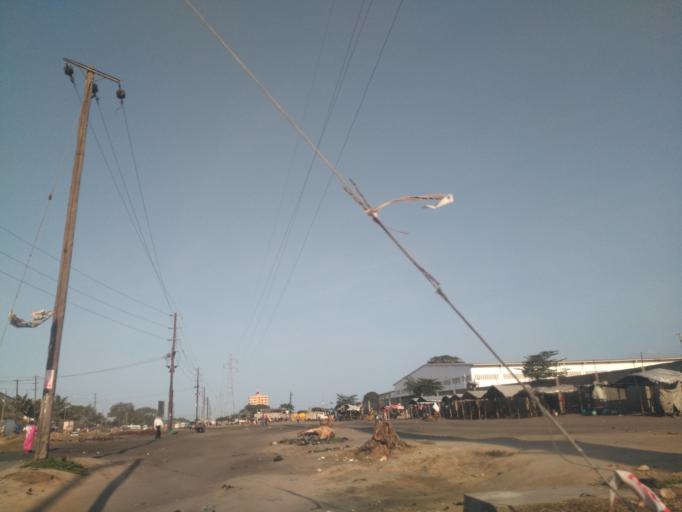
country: TZ
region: Dar es Salaam
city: Dar es Salaam
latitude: -6.9155
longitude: 39.2657
